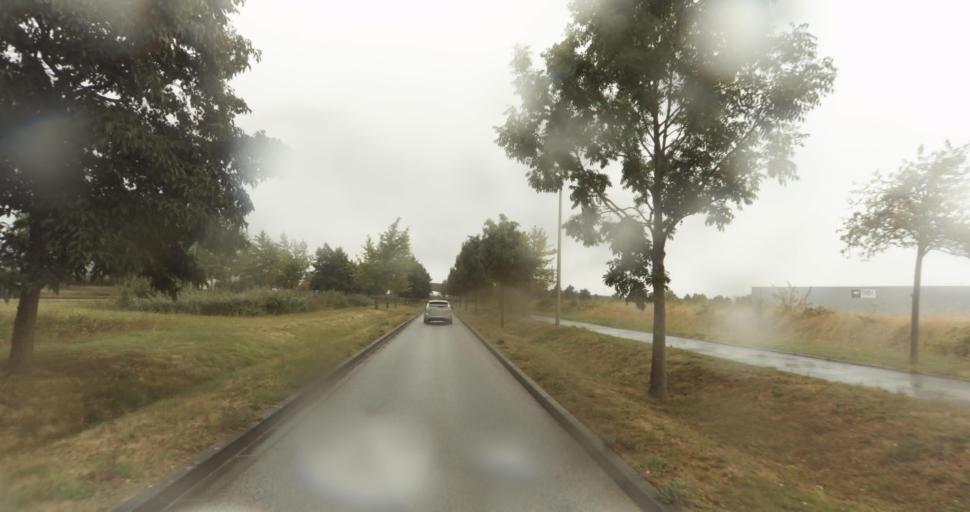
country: FR
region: Haute-Normandie
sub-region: Departement de l'Eure
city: Evreux
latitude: 49.0095
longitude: 1.1809
